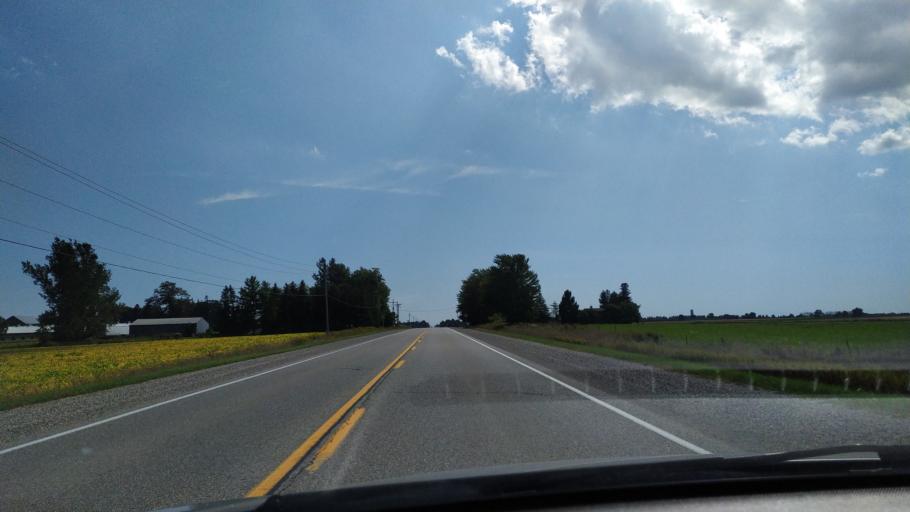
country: CA
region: Ontario
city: Ingersoll
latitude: 43.1257
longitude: -80.8863
